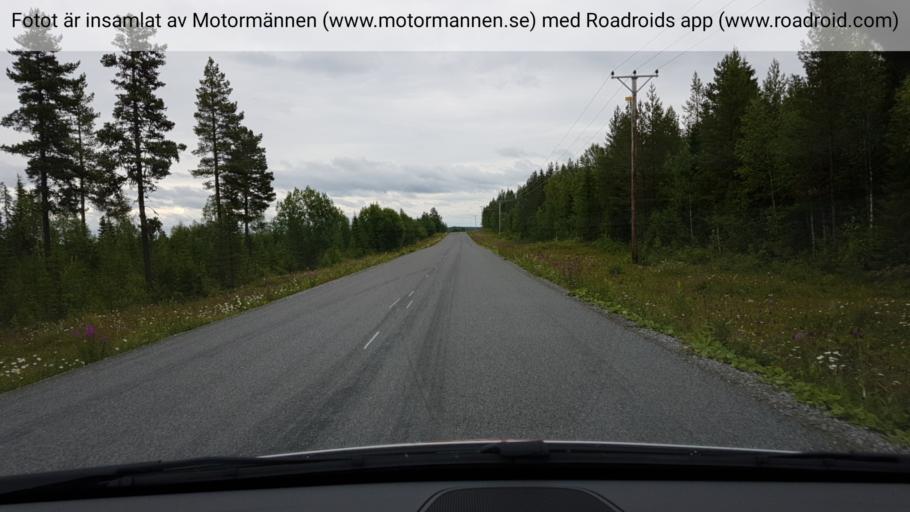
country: SE
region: Jaemtland
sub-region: Krokoms Kommun
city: Krokom
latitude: 63.6658
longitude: 14.5204
